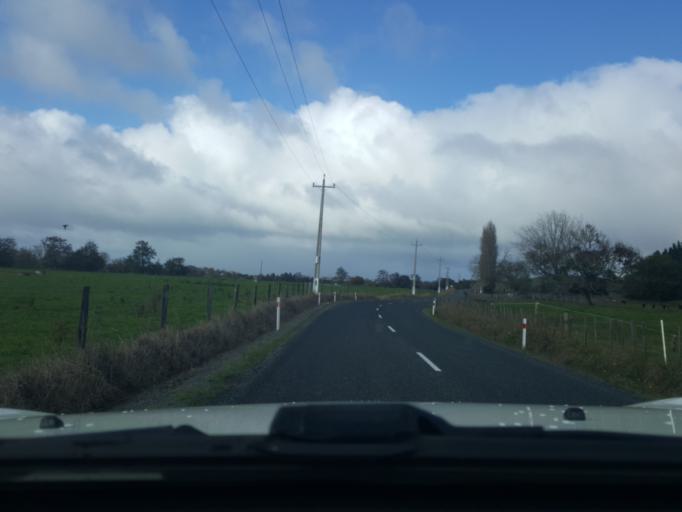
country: NZ
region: Waikato
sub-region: Waikato District
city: Te Kauwhata
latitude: -37.3950
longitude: 175.0575
